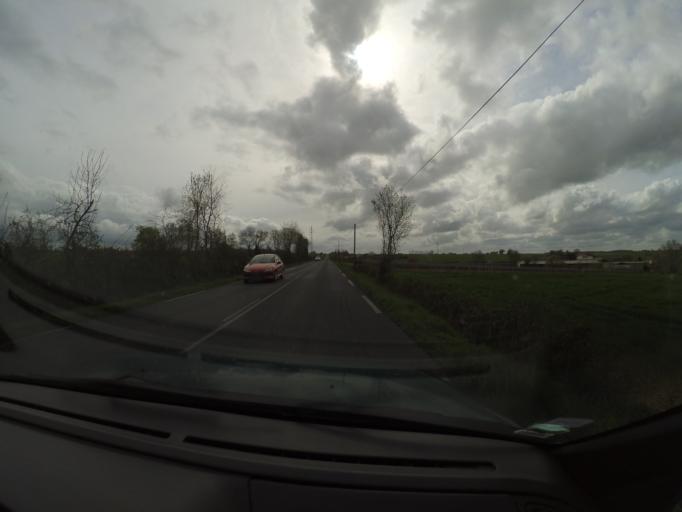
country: FR
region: Pays de la Loire
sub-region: Departement de Maine-et-Loire
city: Saint-Laurent-des-Autels
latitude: 47.2943
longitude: -1.1752
